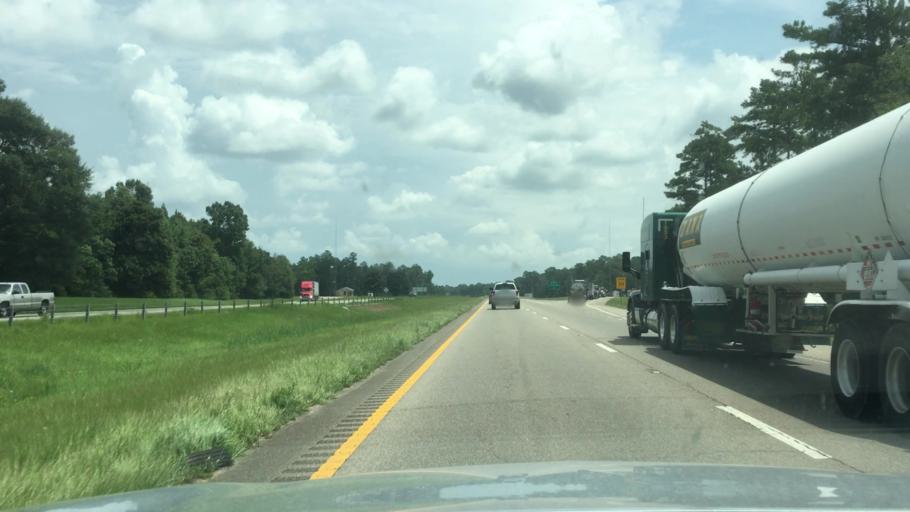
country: US
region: Mississippi
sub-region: Pearl River County
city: Nicholson
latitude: 30.4740
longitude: -89.6837
